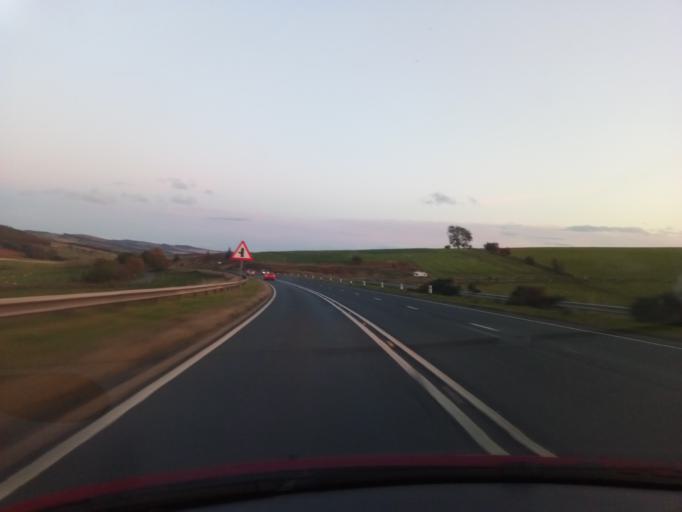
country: GB
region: Scotland
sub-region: The Scottish Borders
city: Lauder
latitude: 55.7892
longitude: -2.8302
